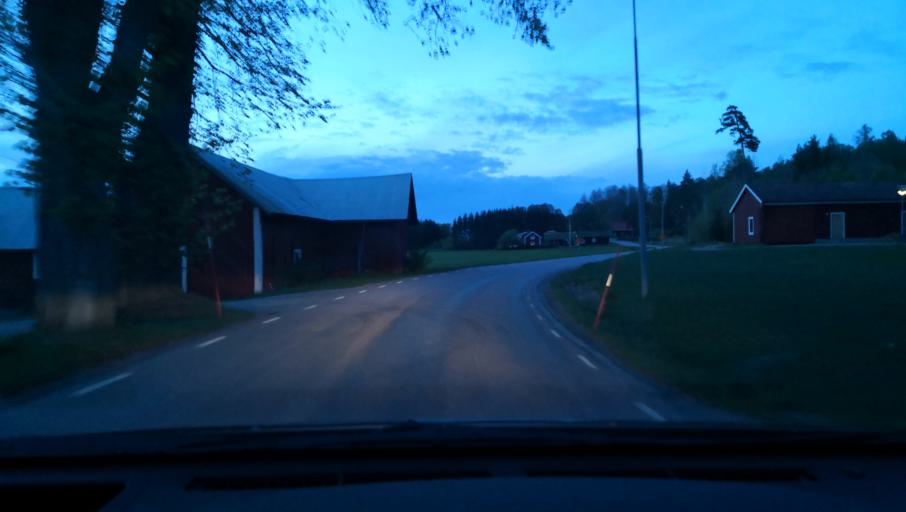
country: SE
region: OErebro
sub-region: Askersunds Kommun
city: Asbro
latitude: 59.0730
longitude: 15.0047
